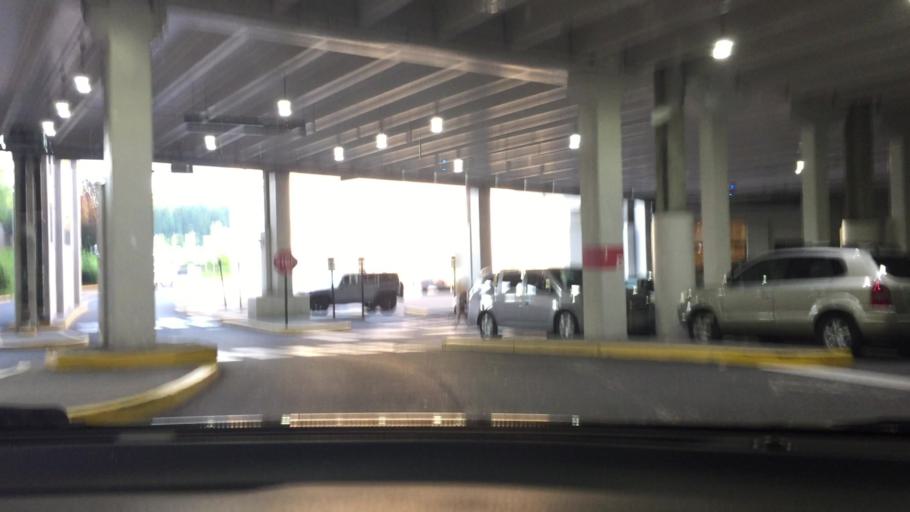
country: US
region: Maryland
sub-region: Montgomery County
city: North Bethesda
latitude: 39.0247
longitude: -77.1479
